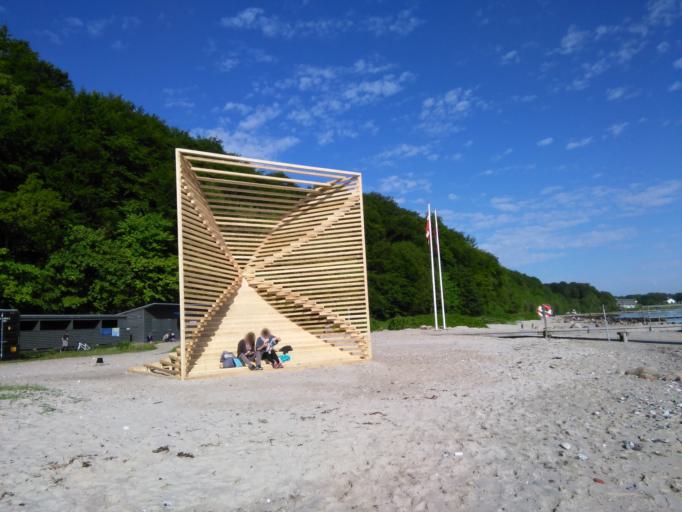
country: DK
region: Central Jutland
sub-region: Arhus Kommune
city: Arhus
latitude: 56.1208
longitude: 10.2263
